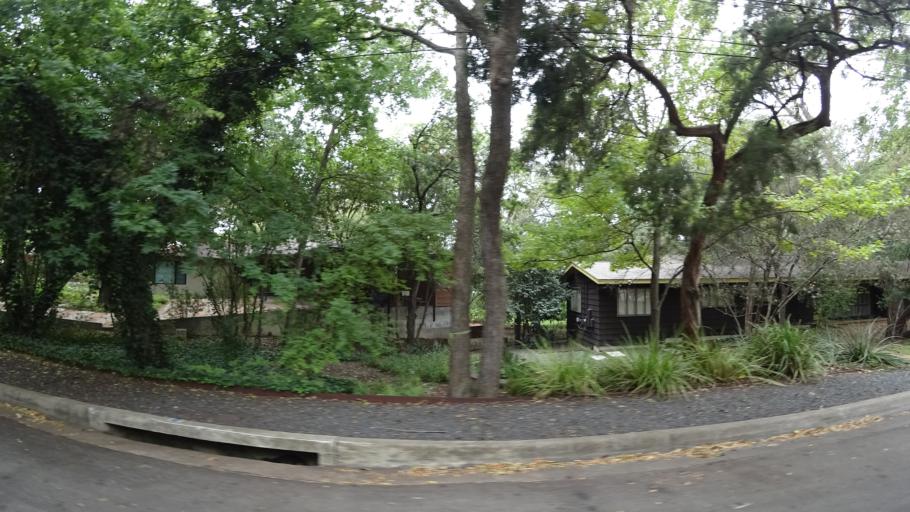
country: US
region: Texas
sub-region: Travis County
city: Austin
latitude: 30.2965
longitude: -97.7267
